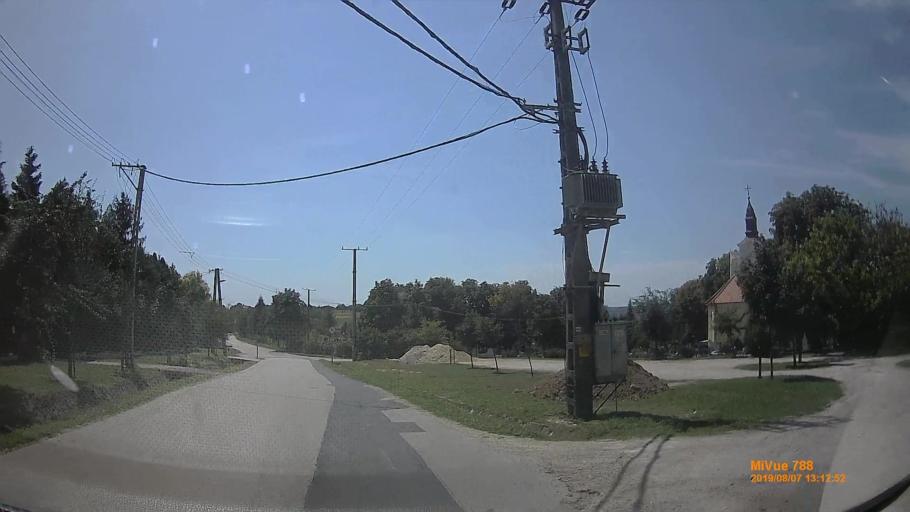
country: HU
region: Zala
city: Cserszegtomaj
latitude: 46.8035
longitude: 17.2201
